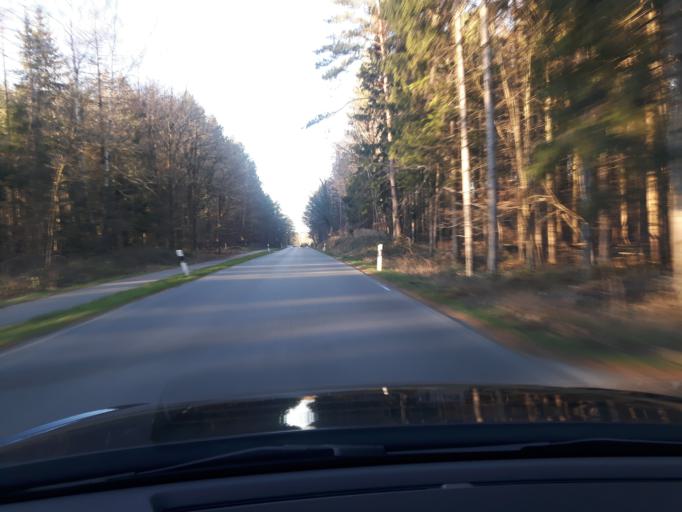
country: DE
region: Mecklenburg-Vorpommern
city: Sehlen
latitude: 54.3794
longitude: 13.3950
